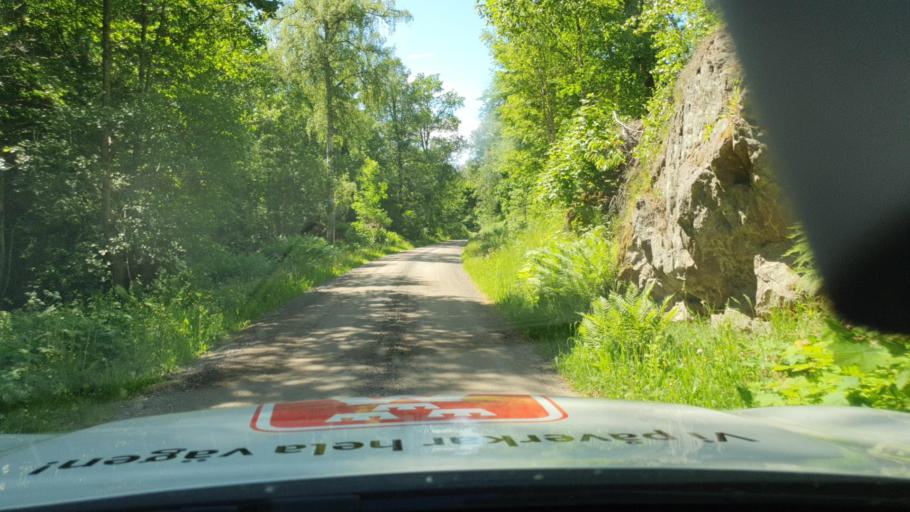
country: SE
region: Joenkoeping
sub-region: Mullsjo Kommun
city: Mullsjoe
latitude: 58.0384
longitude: 13.8768
